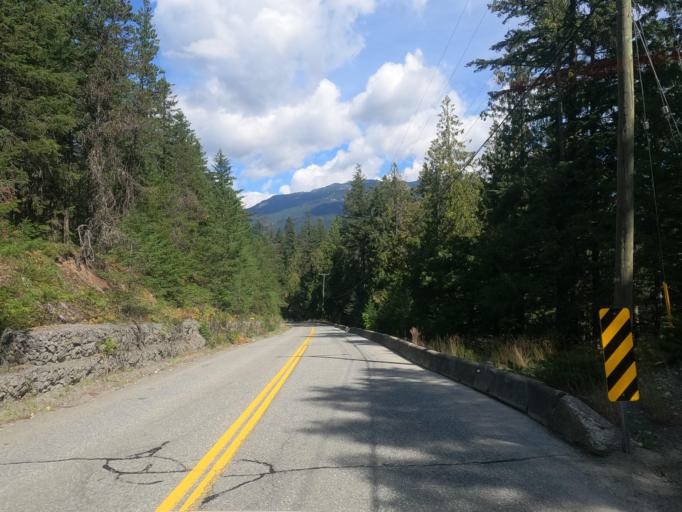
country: CA
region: British Columbia
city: Pemberton
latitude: 50.3401
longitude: -122.7284
